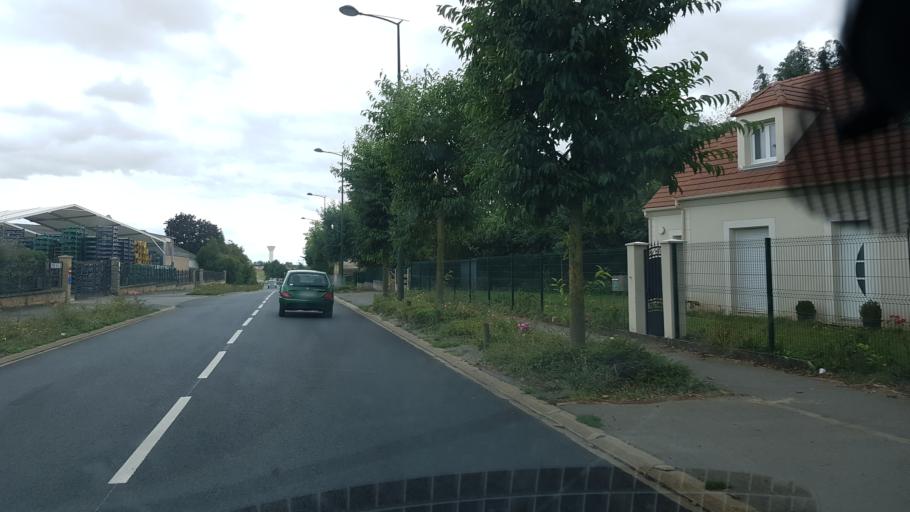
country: FR
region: Centre
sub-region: Departement du Loiret
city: Sermaises
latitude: 48.2928
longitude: 2.2028
